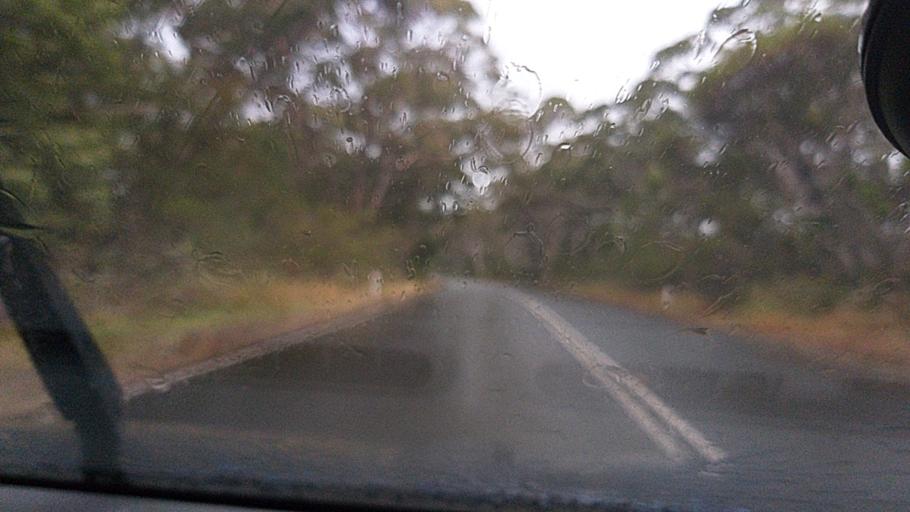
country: AU
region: New South Wales
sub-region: Wollongong
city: Mount Keira
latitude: -34.3799
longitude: 150.8331
